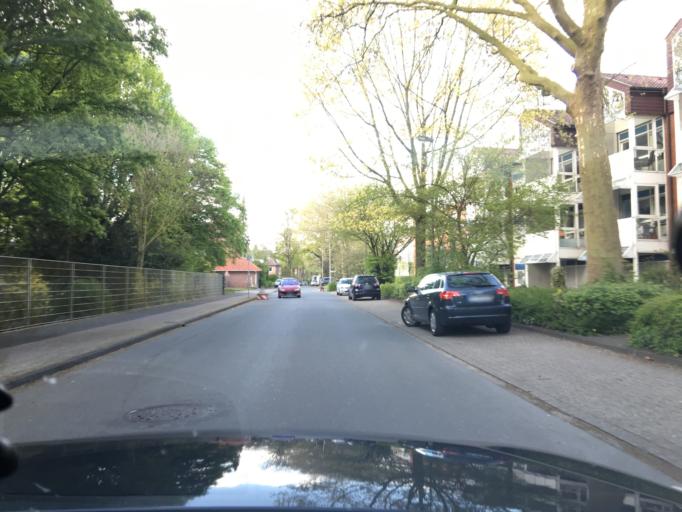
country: DE
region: North Rhine-Westphalia
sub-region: Regierungsbezirk Munster
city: Muenster
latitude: 51.9606
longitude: 7.6535
